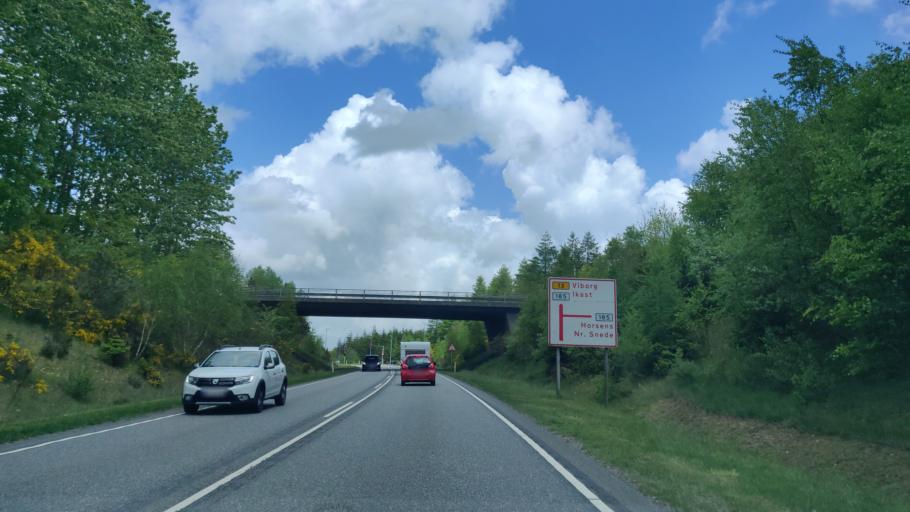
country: DK
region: Central Jutland
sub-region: Hedensted Kommune
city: Torring
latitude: 55.9602
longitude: 9.4040
